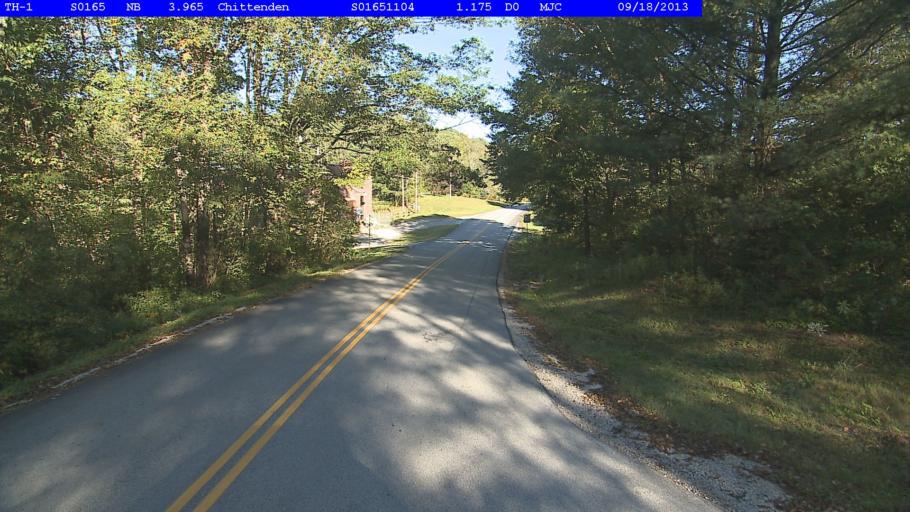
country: US
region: Vermont
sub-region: Rutland County
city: Rutland
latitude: 43.6935
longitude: -72.9542
